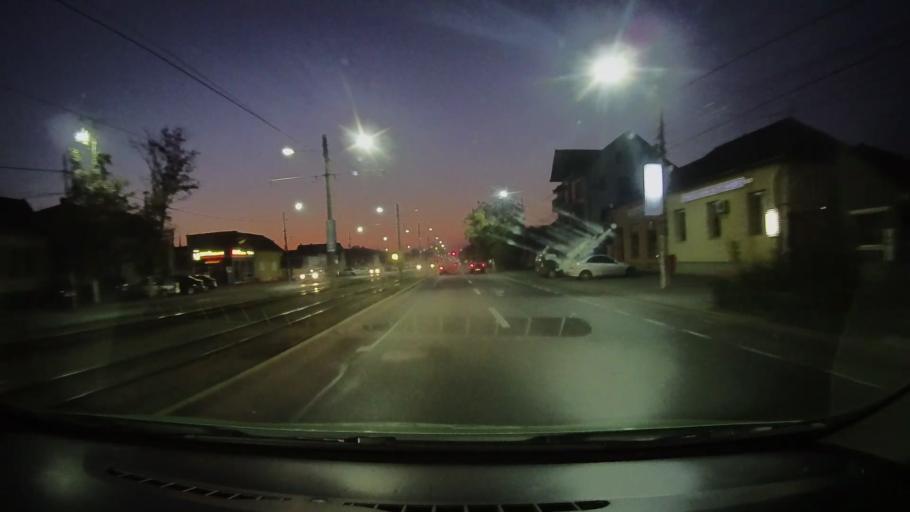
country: RO
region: Arad
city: Arad
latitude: 46.1772
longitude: 21.3580
